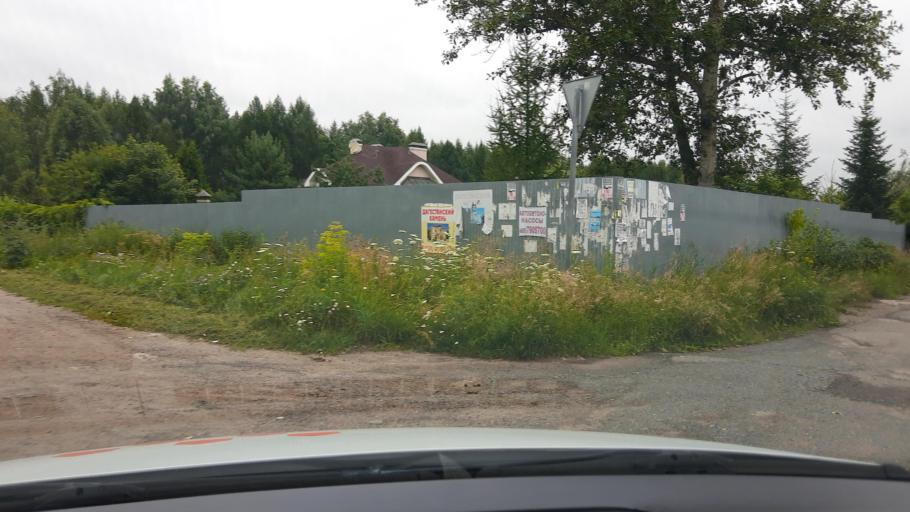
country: RU
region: Moskovskaya
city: Gorki-Leninskiye
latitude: 55.4975
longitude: 37.8251
